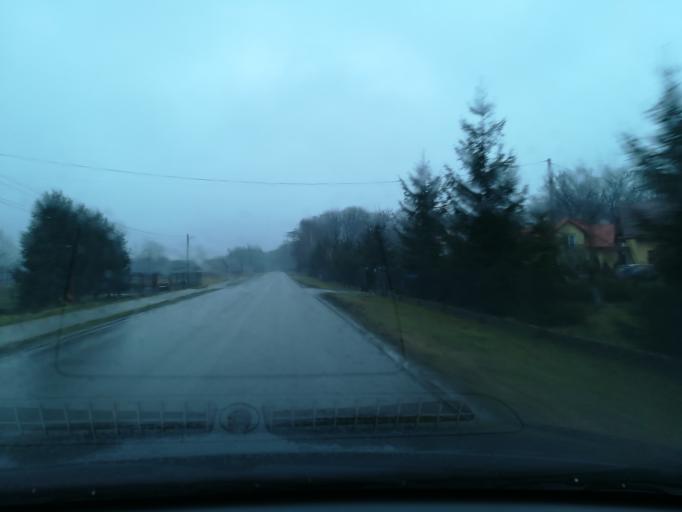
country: PL
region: Subcarpathian Voivodeship
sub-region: Powiat lancucki
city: Bialobrzegi
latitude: 50.1171
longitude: 22.3435
